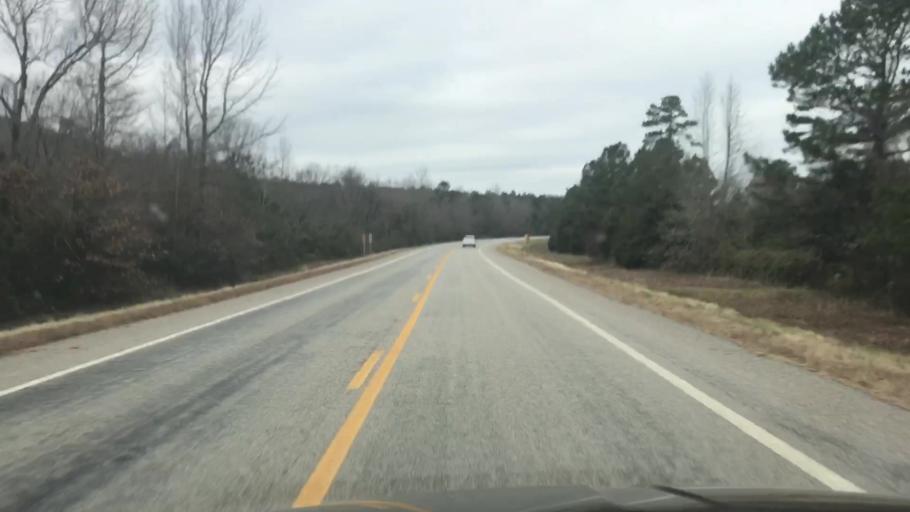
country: US
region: Arkansas
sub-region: Scott County
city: Waldron
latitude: 34.7038
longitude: -93.9245
